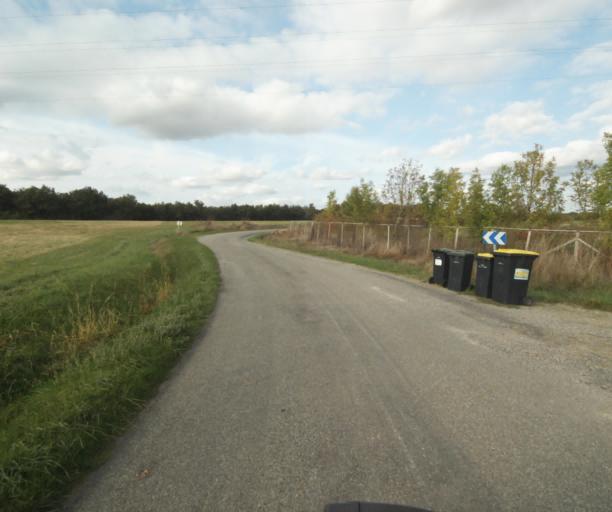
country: FR
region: Midi-Pyrenees
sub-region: Departement du Tarn-et-Garonne
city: Verdun-sur-Garonne
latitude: 43.8417
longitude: 1.1613
